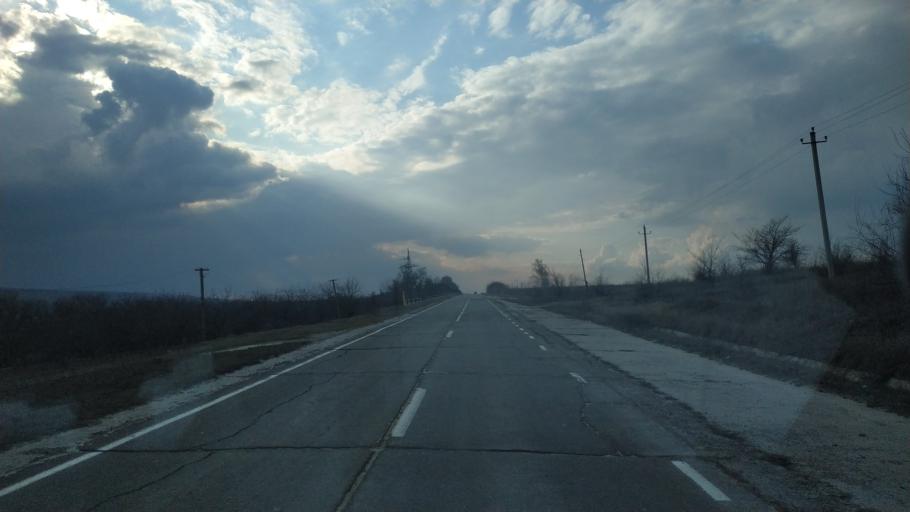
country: MD
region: Anenii Noi
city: Varnita
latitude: 46.9243
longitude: 29.4380
